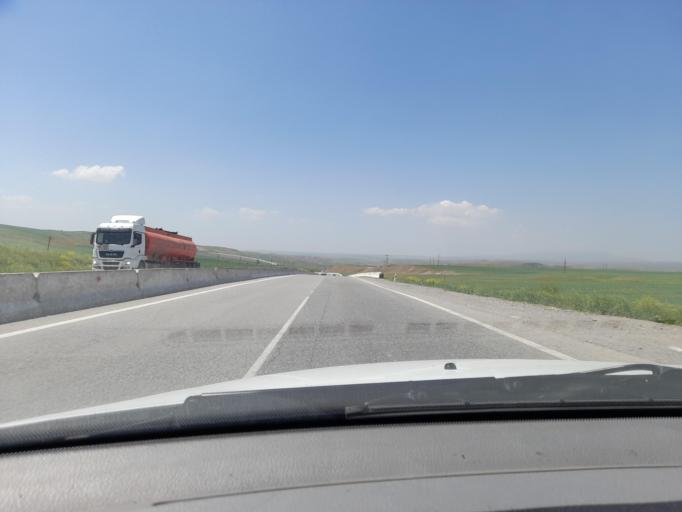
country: UZ
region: Jizzax
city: Jizzax
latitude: 40.0535
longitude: 67.7287
